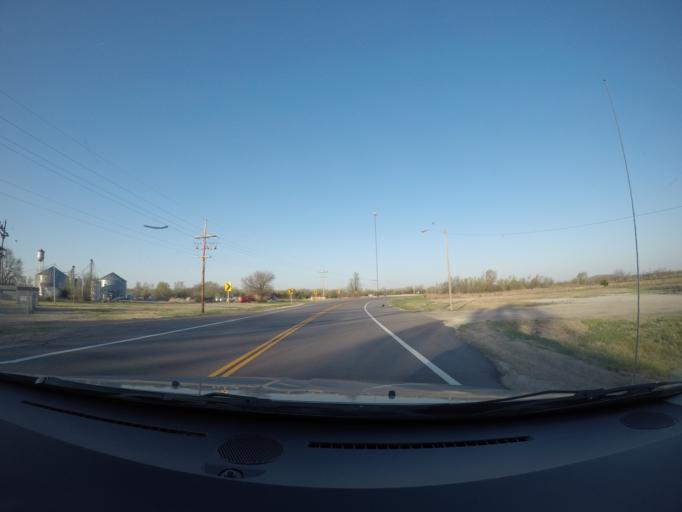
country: US
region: Kansas
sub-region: Stafford County
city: Stafford
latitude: 37.8095
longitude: -98.4313
